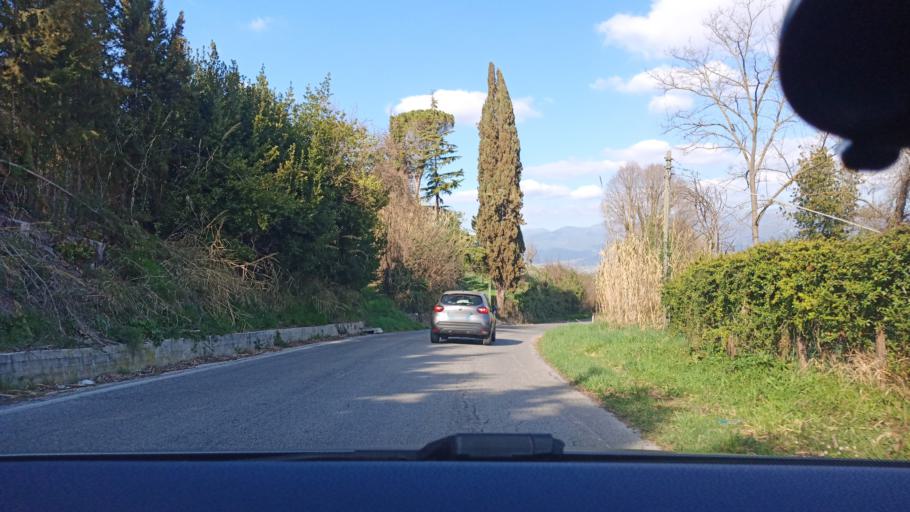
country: IT
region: Latium
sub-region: Citta metropolitana di Roma Capitale
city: Torrita Tiberina
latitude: 42.2414
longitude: 12.6168
